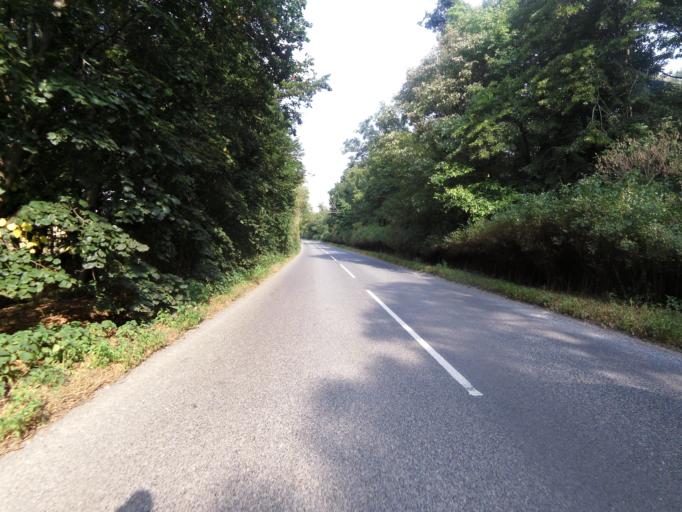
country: GB
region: England
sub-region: Suffolk
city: Bramford
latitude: 52.1291
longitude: 1.1004
